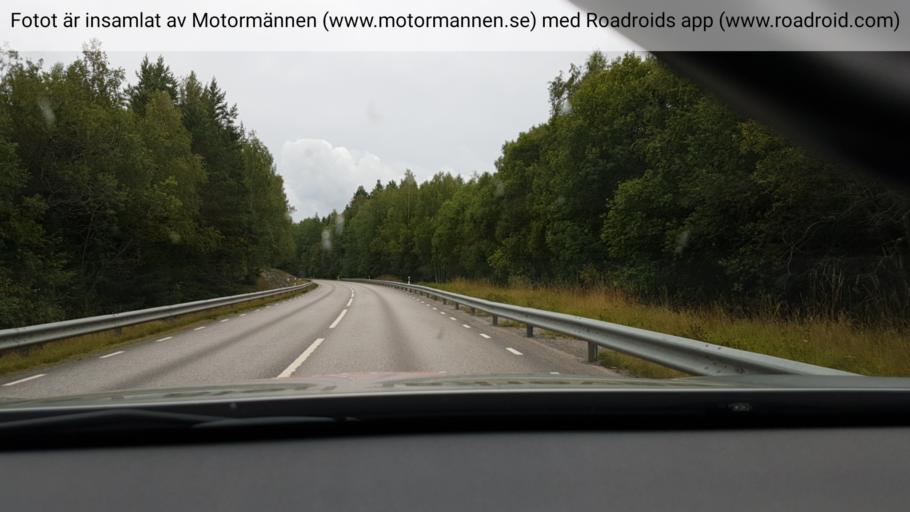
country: SE
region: Stockholm
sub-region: Vallentuna Kommun
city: Vallentuna
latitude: 59.7277
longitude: 18.0536
